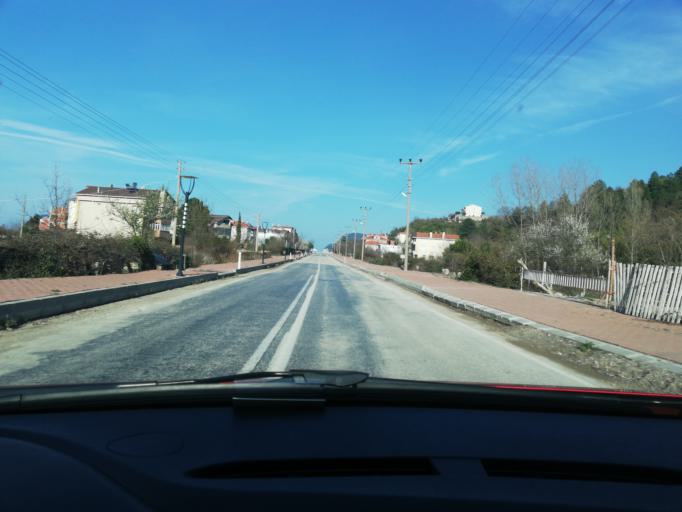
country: TR
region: Kastamonu
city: Cide
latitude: 41.8804
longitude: 32.9428
